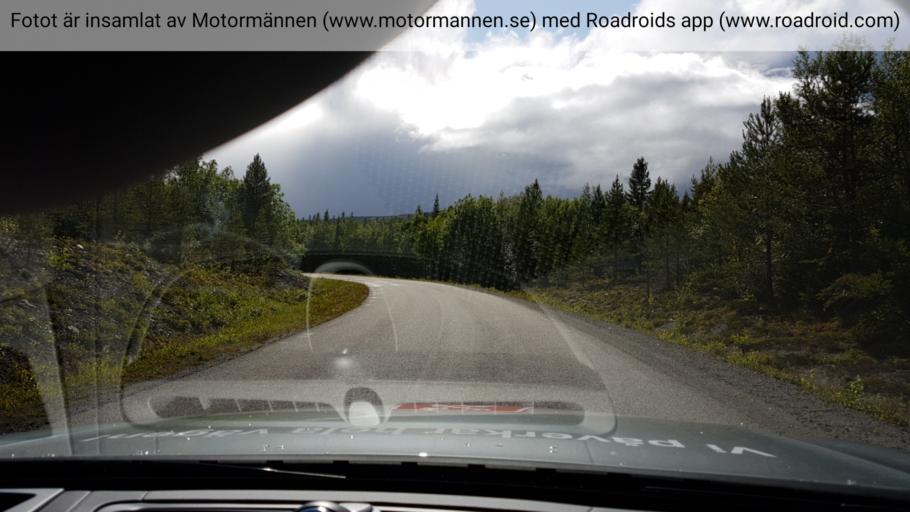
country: SE
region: Jaemtland
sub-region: Bergs Kommun
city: Hoverberg
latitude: 63.0432
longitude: 13.9690
